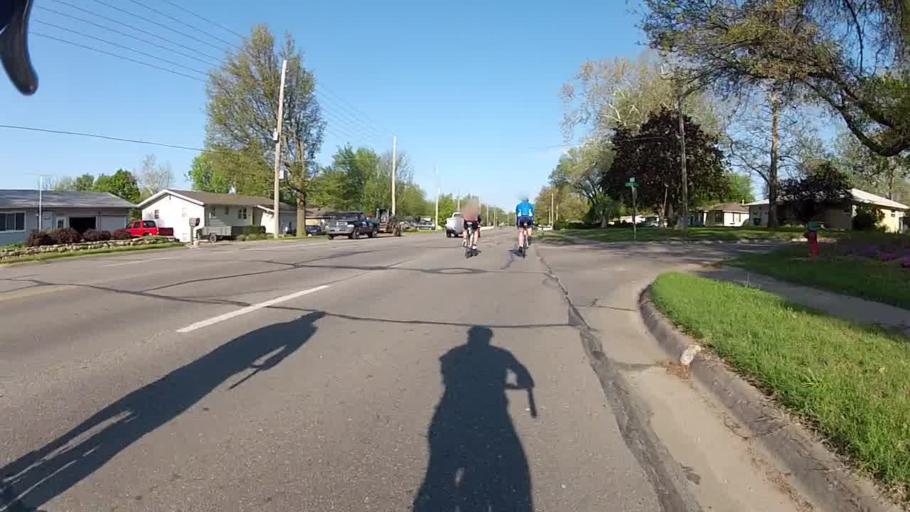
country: US
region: Kansas
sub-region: Riley County
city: Manhattan
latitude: 39.1890
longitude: -96.6228
